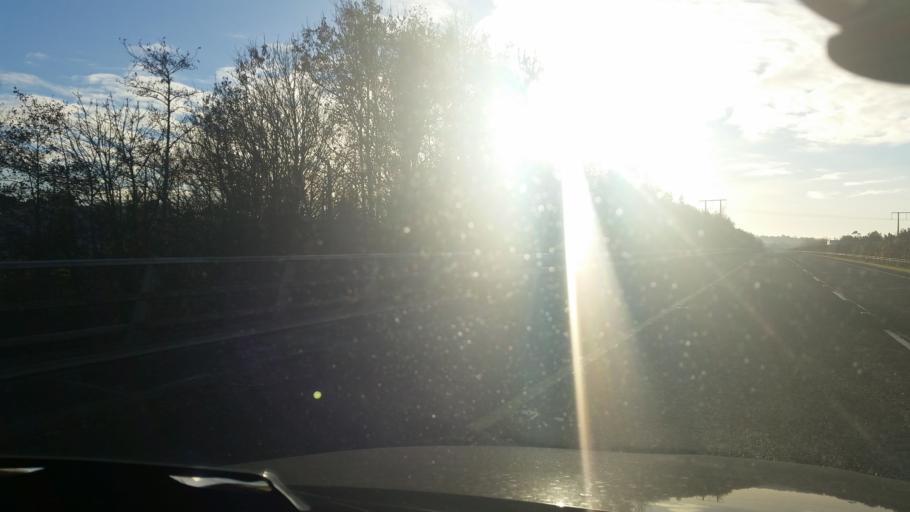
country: IE
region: Leinster
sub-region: Wicklow
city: Arklow
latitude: 52.7943
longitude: -6.1820
